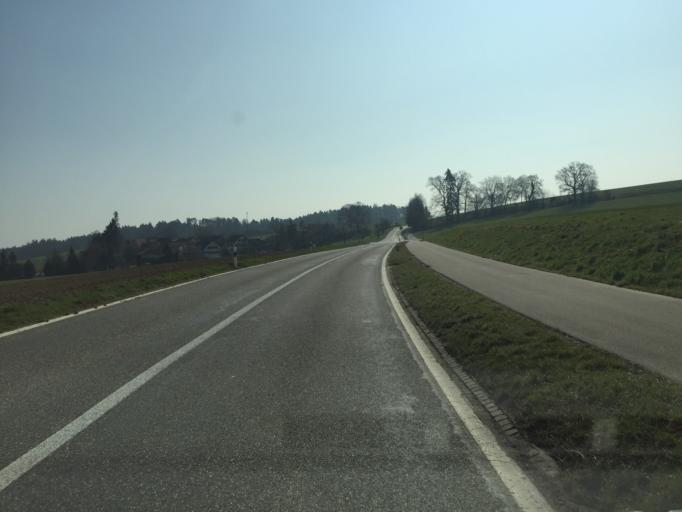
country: CH
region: Thurgau
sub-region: Frauenfeld District
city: Huttwilen
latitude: 47.5978
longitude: 8.8880
